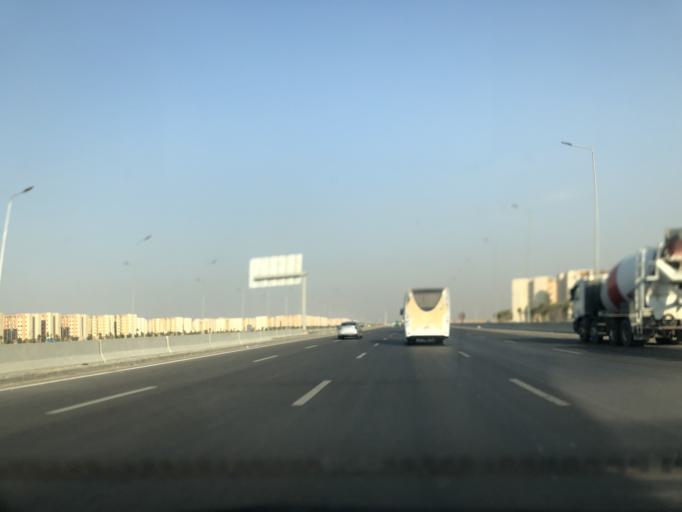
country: EG
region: Al Jizah
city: Madinat Sittah Uktubar
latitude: 29.9061
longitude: 30.9465
